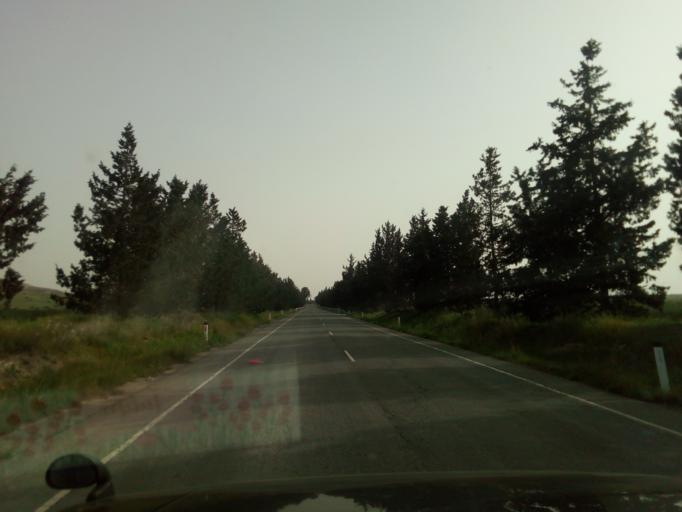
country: CY
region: Lefkosia
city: Lympia
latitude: 35.0193
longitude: 33.4952
